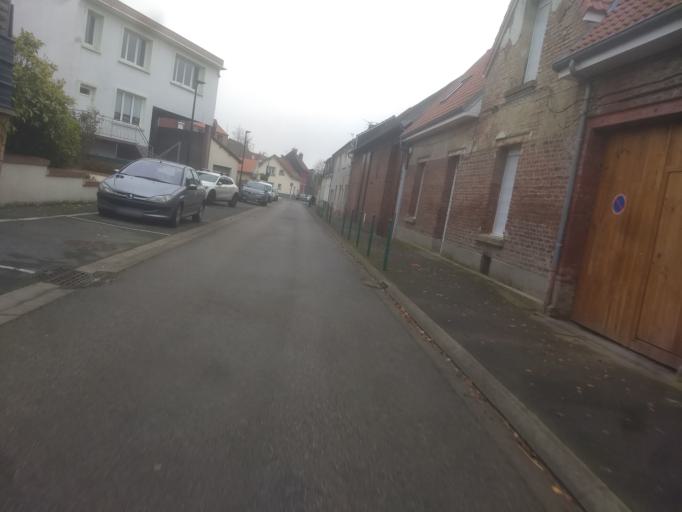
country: FR
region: Nord-Pas-de-Calais
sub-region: Departement du Pas-de-Calais
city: Saint-Laurent-Blangy
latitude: 50.3041
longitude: 2.8095
